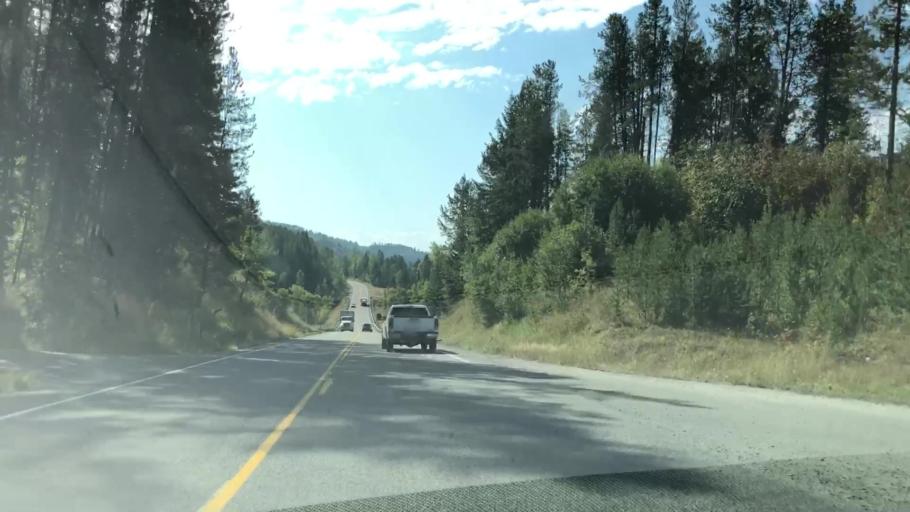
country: US
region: Idaho
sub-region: Teton County
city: Victor
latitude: 43.2859
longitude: -111.1210
